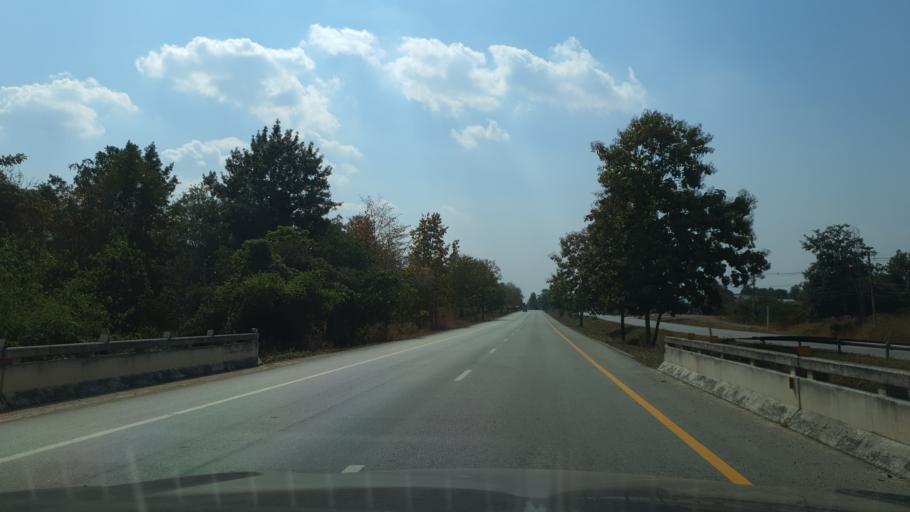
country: TH
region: Tak
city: Sam Ngao
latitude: 17.3007
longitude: 99.1459
